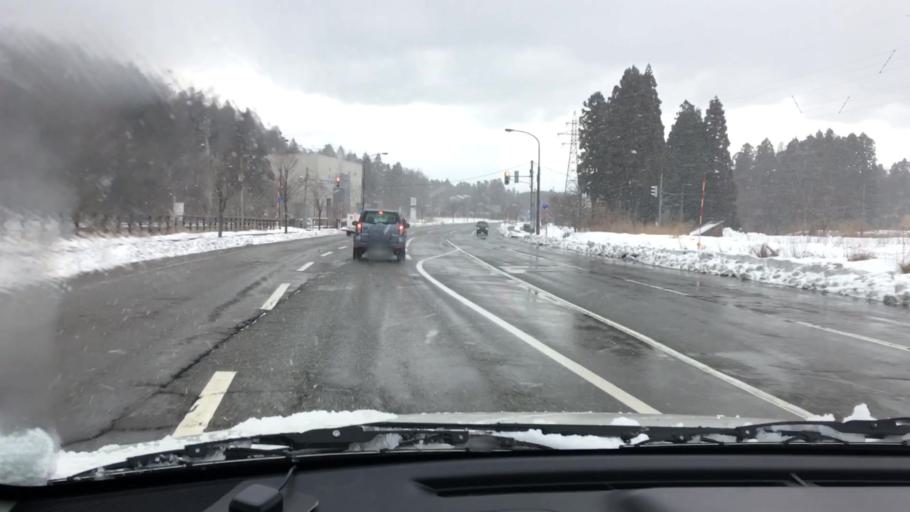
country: JP
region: Niigata
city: Joetsu
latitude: 37.0973
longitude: 138.2310
